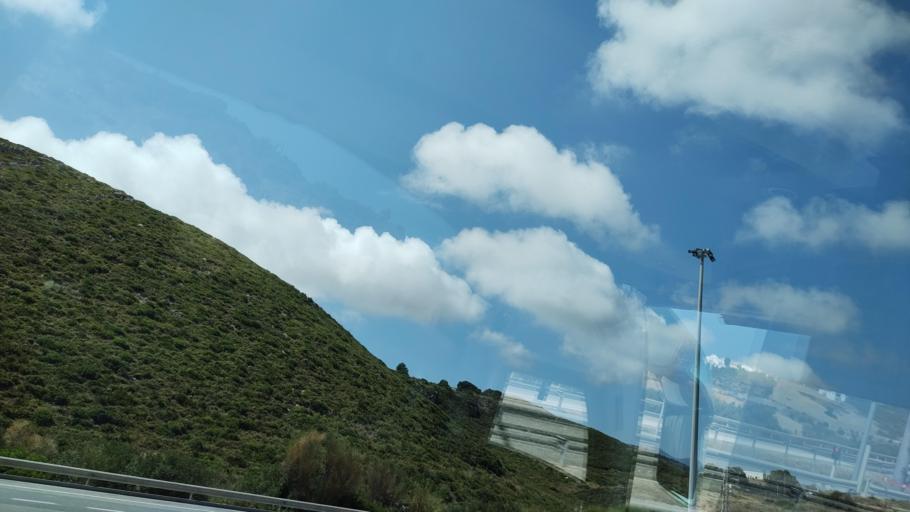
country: ES
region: Andalusia
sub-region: Provincia de Malaga
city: Manilva
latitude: 36.3752
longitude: -5.2658
